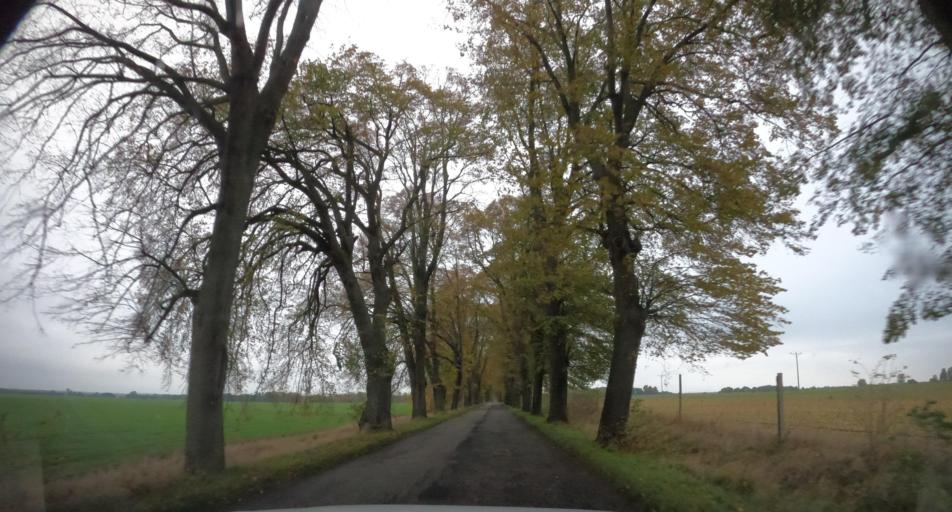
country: PL
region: West Pomeranian Voivodeship
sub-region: Powiat kamienski
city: Wolin
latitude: 53.9002
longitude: 14.6285
